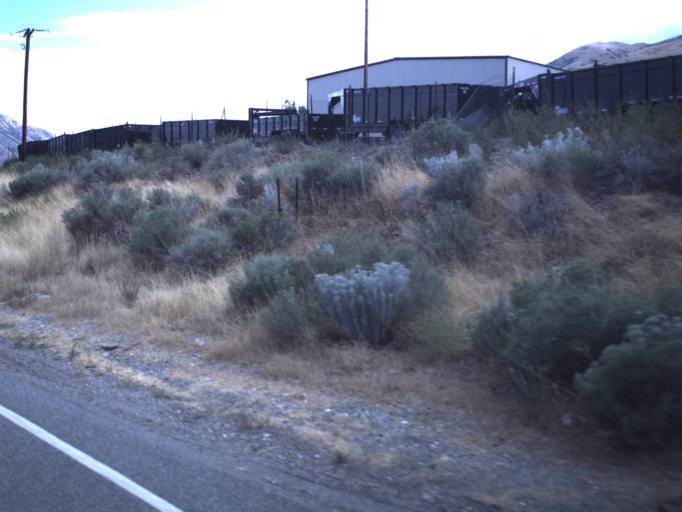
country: US
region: Utah
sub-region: Box Elder County
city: Perry
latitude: 41.4596
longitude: -112.0372
